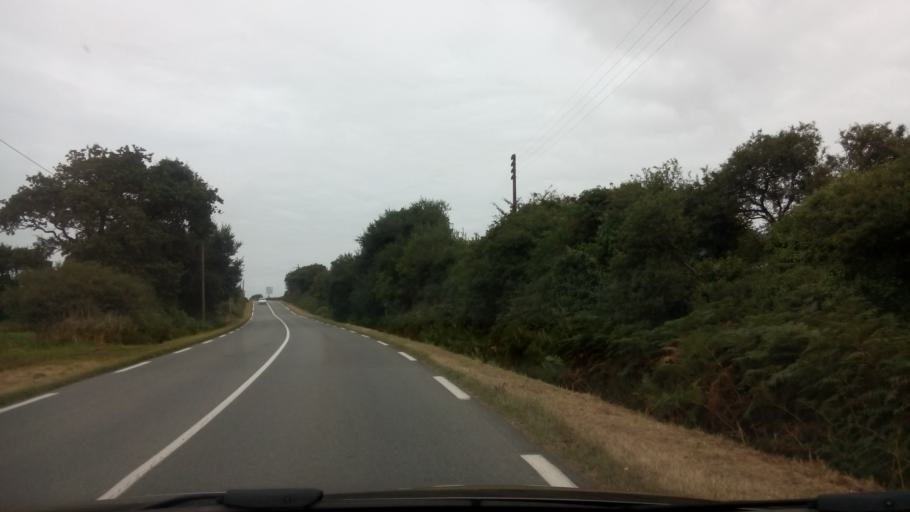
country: FR
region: Brittany
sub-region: Departement des Cotes-d'Armor
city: Ploumilliau
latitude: 48.6948
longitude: -3.5478
